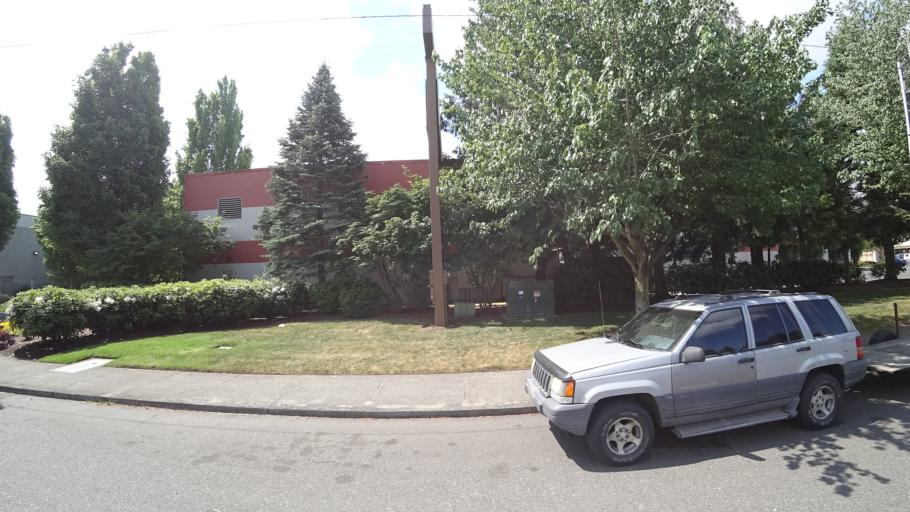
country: US
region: Washington
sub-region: Clark County
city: Vancouver
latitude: 45.6153
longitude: -122.6858
